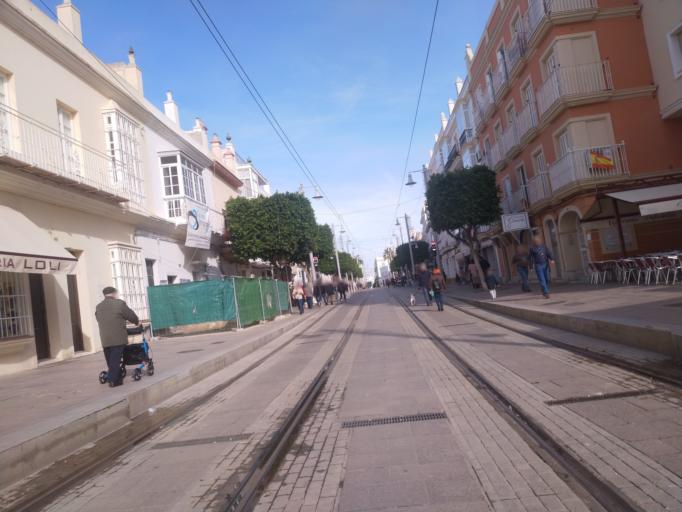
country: ES
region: Andalusia
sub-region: Provincia de Cadiz
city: San Fernando
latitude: 36.4606
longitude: -6.2009
